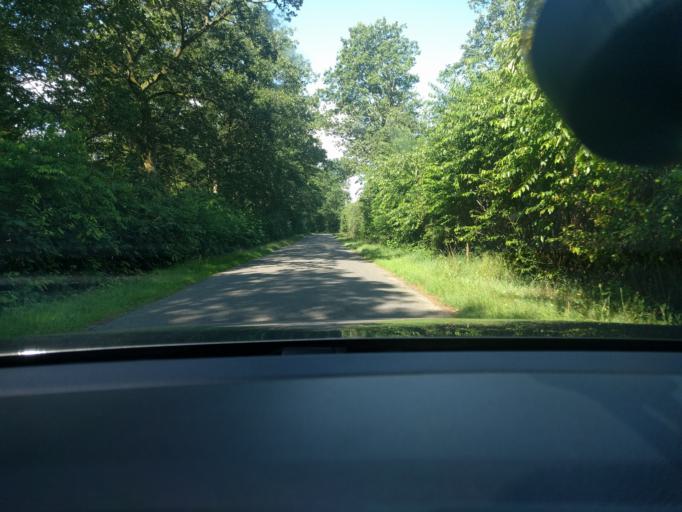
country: DK
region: Central Jutland
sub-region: Viborg Kommune
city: Viborg
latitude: 56.4133
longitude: 9.3570
